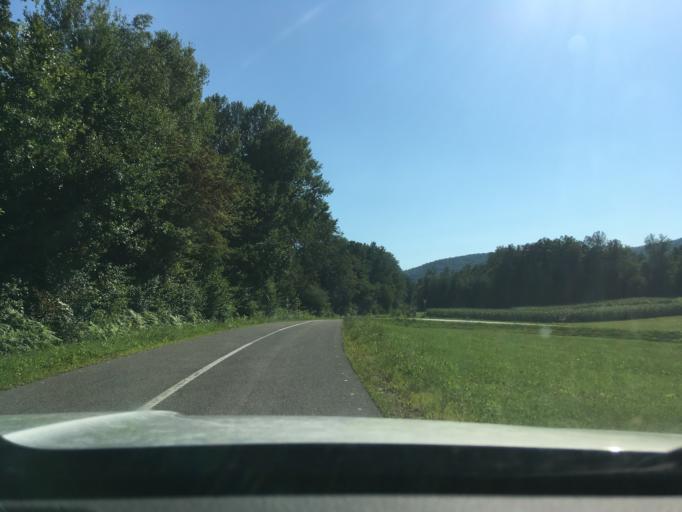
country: SI
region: Crnomelj
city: Crnomelj
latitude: 45.4561
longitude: 15.2181
